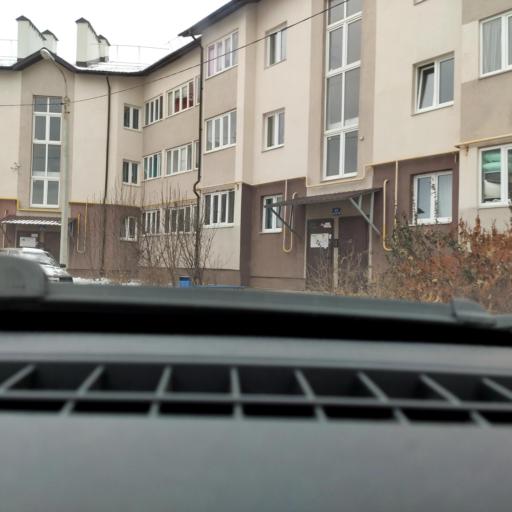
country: RU
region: Bashkortostan
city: Avdon
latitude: 54.6976
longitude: 55.8050
